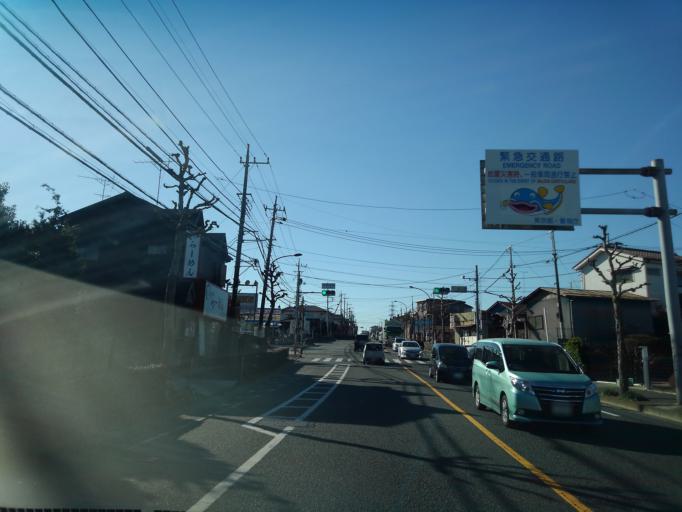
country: JP
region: Tokyo
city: Hino
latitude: 35.6798
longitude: 139.3664
